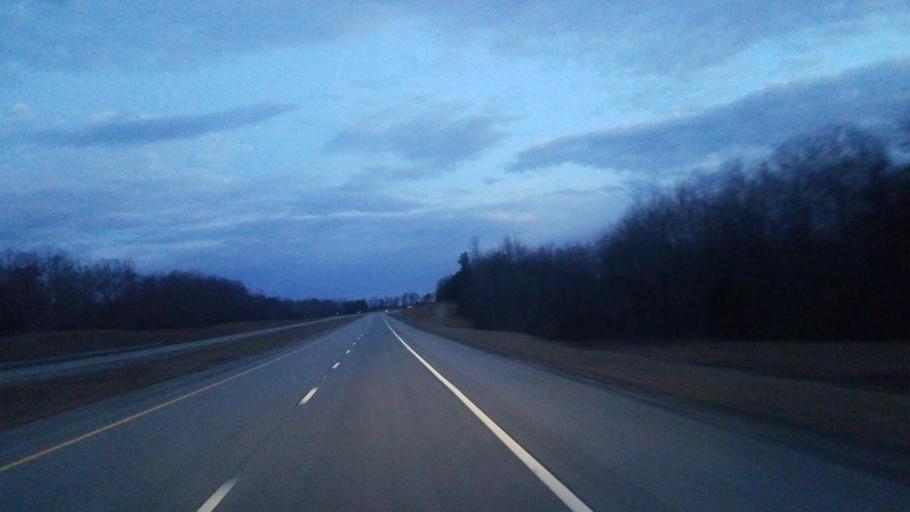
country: US
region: Tennessee
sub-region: Van Buren County
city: Spencer
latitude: 35.6171
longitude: -85.4741
